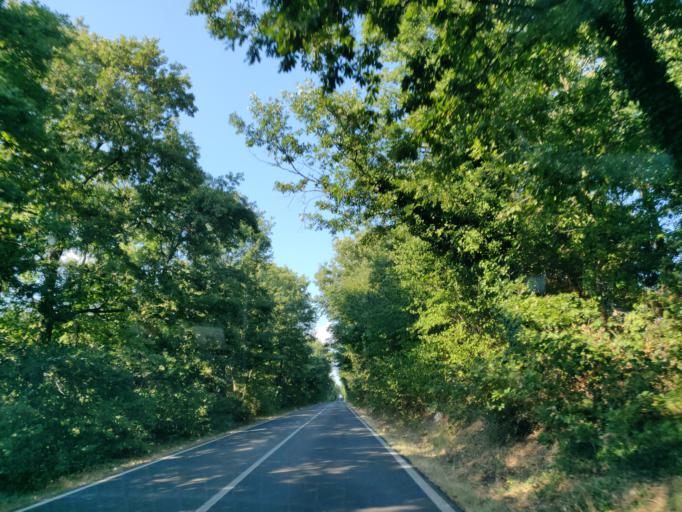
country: IT
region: Latium
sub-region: Provincia di Viterbo
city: Latera
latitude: 42.5978
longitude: 11.8396
